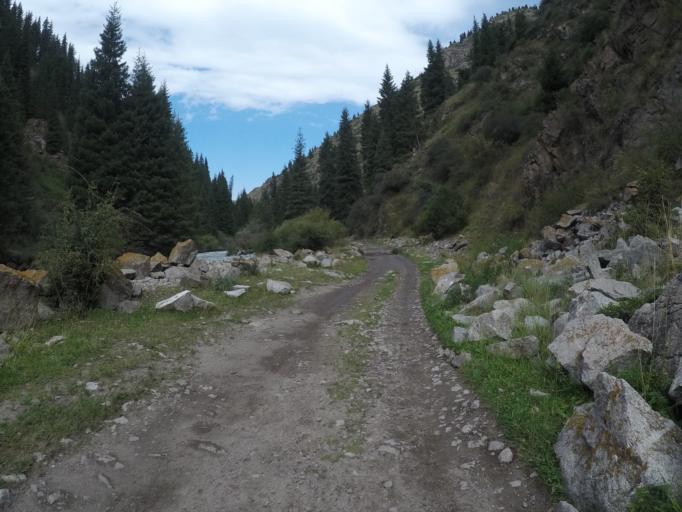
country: KG
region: Ysyk-Koel
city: Teploklyuchenka
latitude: 42.4405
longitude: 78.5570
